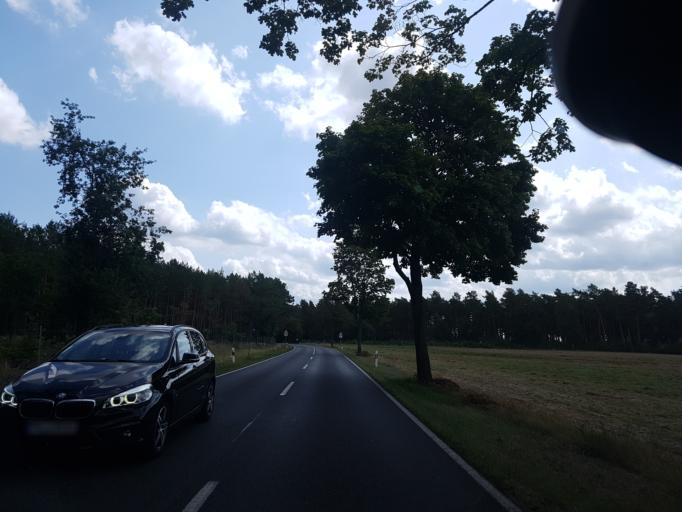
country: DE
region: Brandenburg
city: Borkwalde
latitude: 52.3018
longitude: 12.7967
